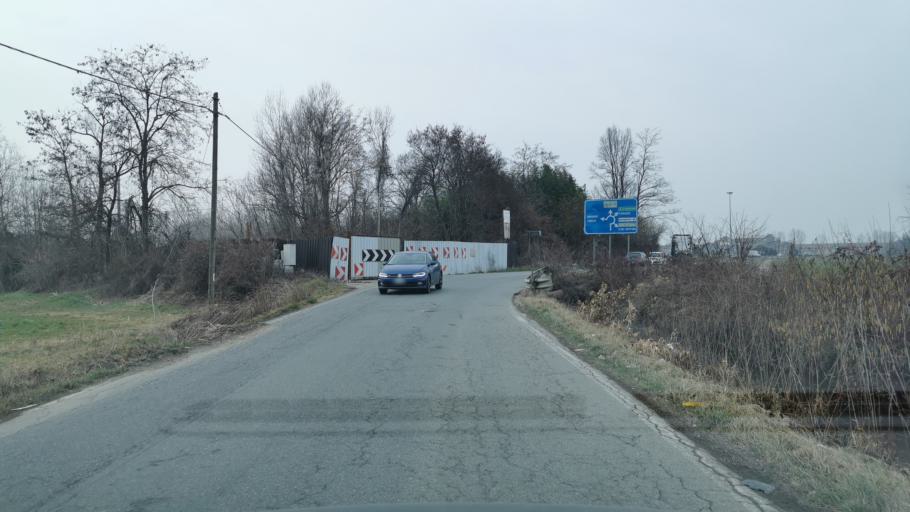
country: IT
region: Piedmont
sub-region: Provincia di Torino
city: Borgaro Torinese
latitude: 45.1378
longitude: 7.6854
